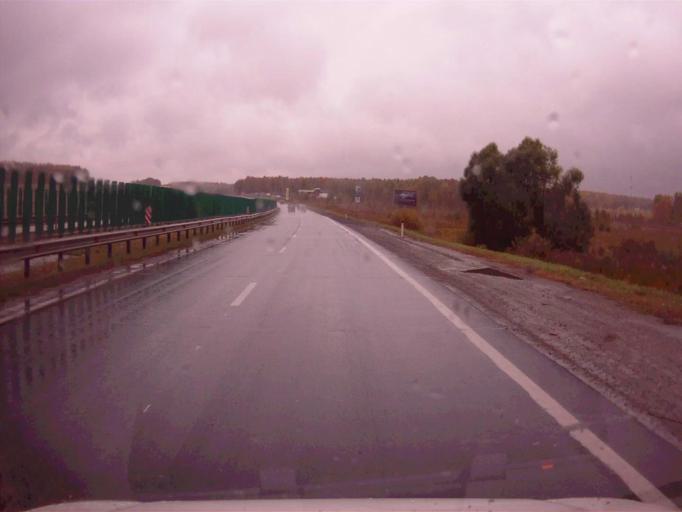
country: RU
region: Chelyabinsk
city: Dolgoderevenskoye
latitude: 55.3217
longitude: 61.3334
